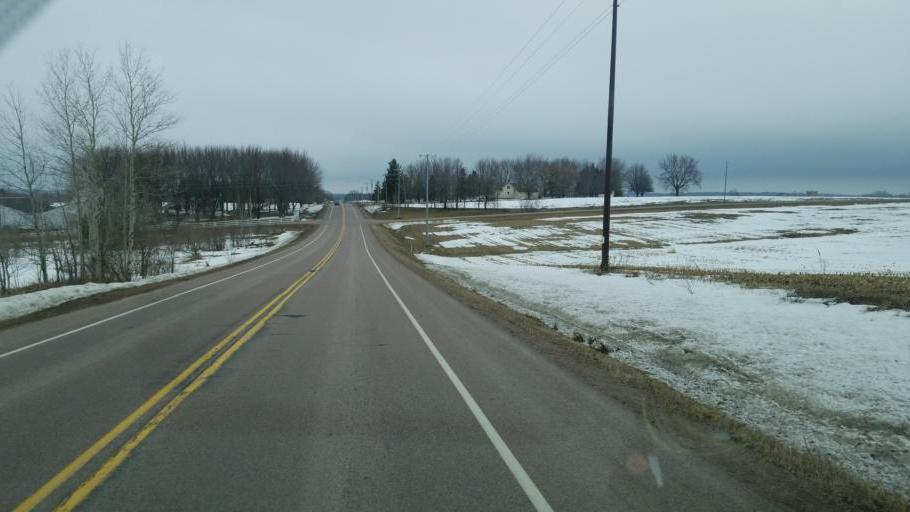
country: US
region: Wisconsin
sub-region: Wood County
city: Marshfield
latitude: 44.6329
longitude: -90.2183
